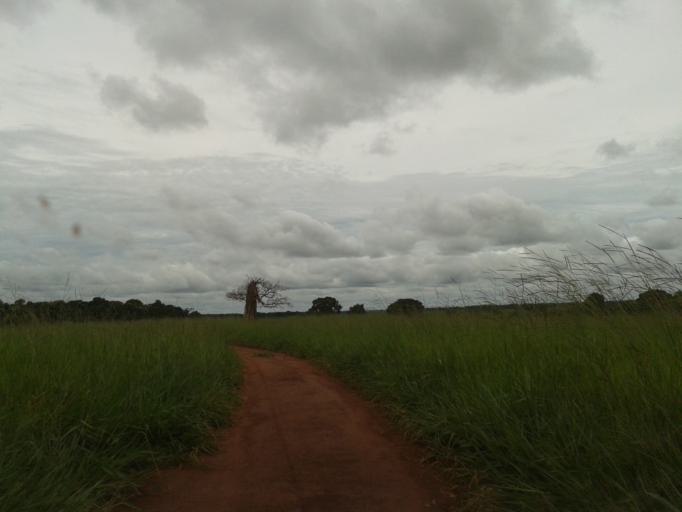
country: BR
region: Minas Gerais
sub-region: Capinopolis
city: Capinopolis
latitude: -18.7832
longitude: -49.7806
